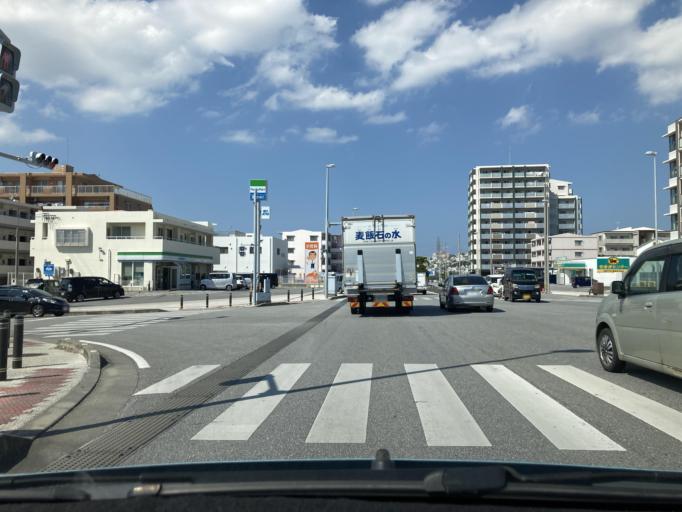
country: JP
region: Okinawa
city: Tomigusuku
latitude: 26.1901
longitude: 127.7162
